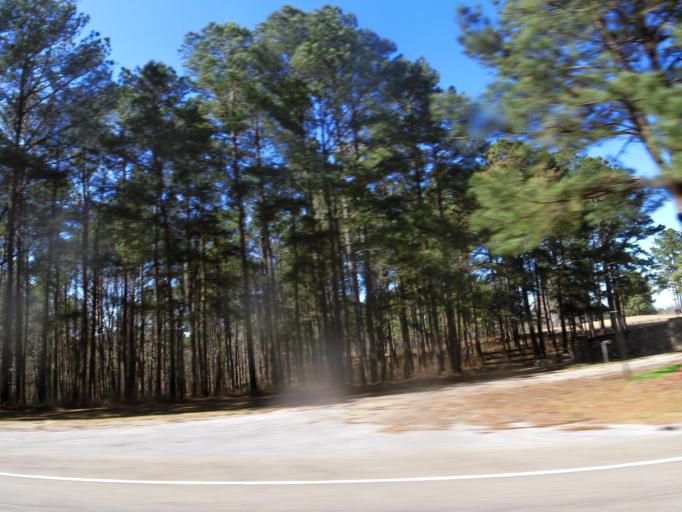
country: US
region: Alabama
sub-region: Bullock County
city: Union Springs
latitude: 32.1299
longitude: -85.7691
